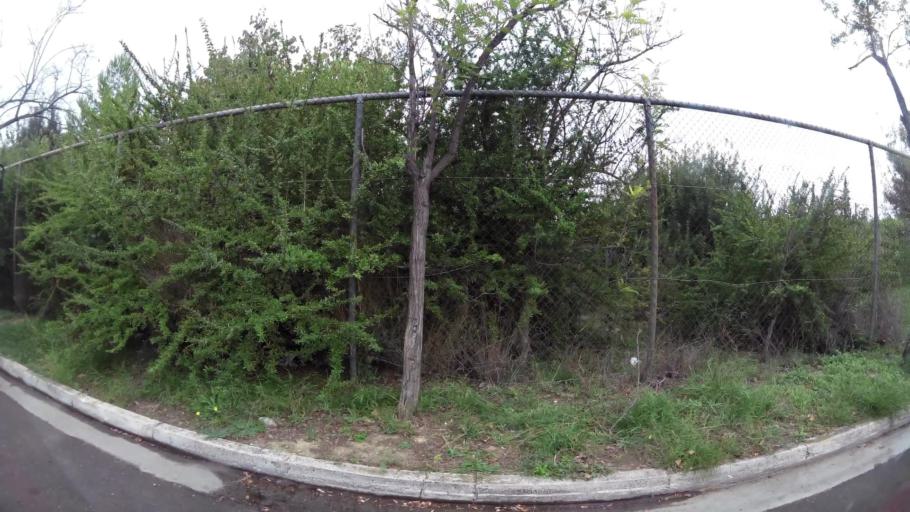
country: GR
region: Attica
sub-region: Nomarchia Athinas
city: Agioi Anargyroi
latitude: 38.0341
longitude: 23.7179
